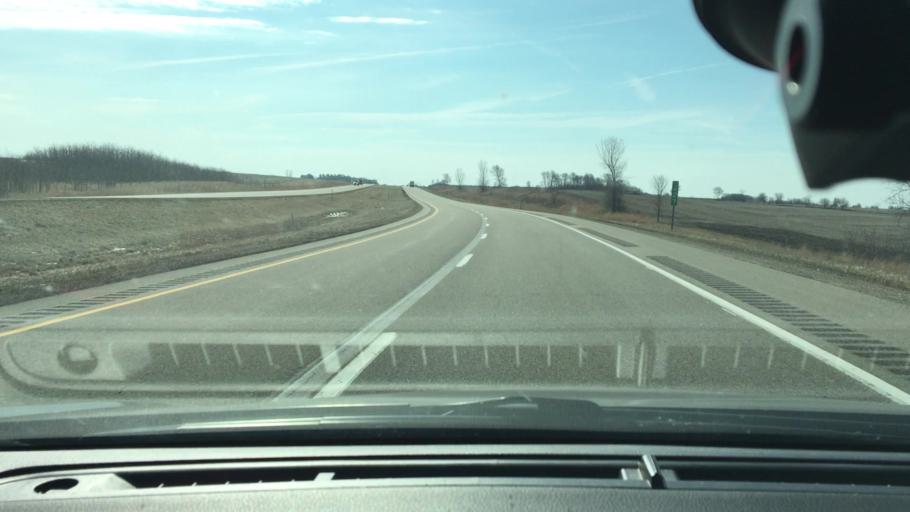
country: US
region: Iowa
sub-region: Floyd County
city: Charles City
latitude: 43.0209
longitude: -92.6475
